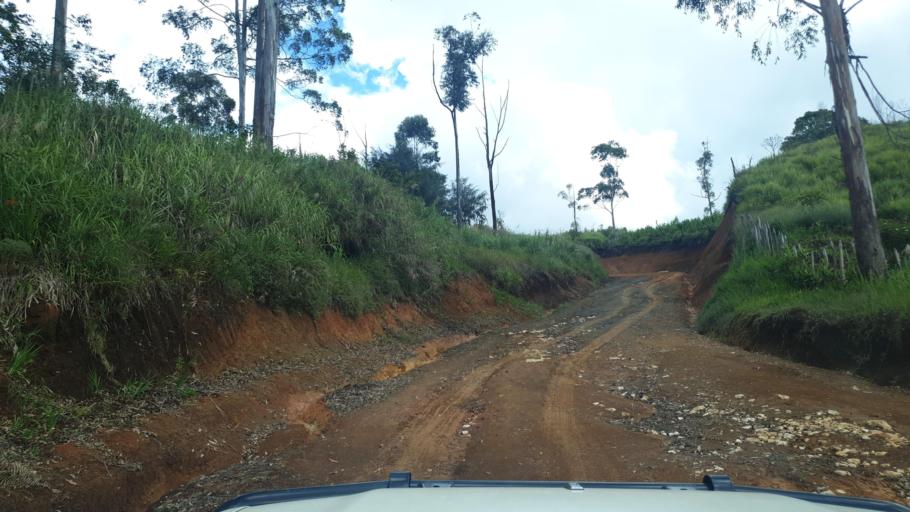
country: PG
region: Eastern Highlands
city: Goroka
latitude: -6.2784
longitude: 145.1913
